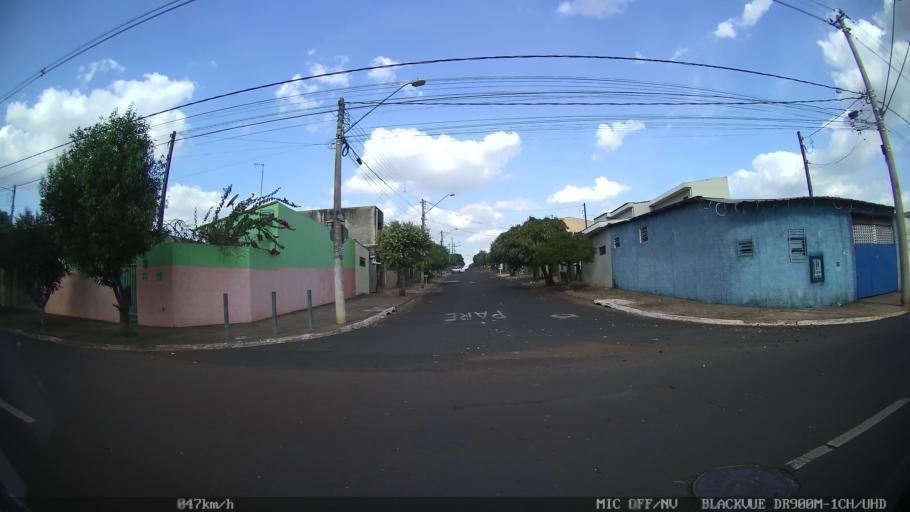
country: BR
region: Sao Paulo
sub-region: Ribeirao Preto
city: Ribeirao Preto
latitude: -21.1952
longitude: -47.8493
